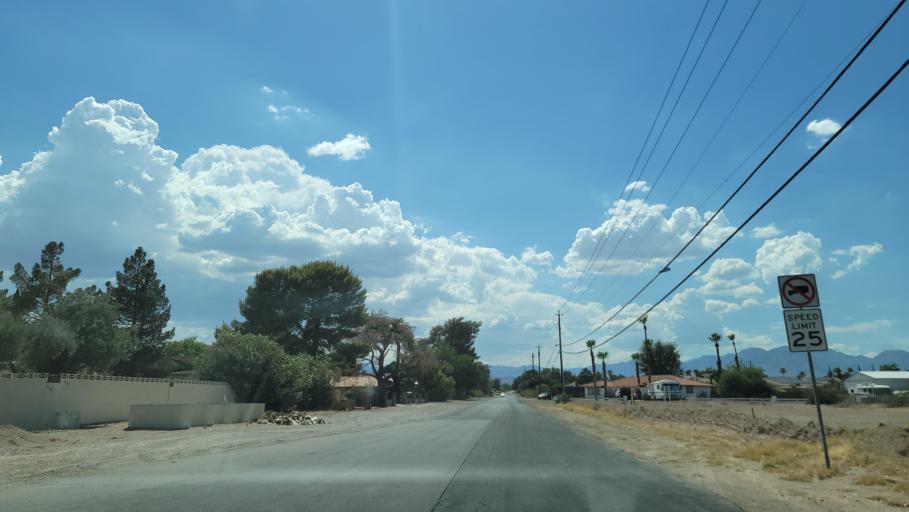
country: US
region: Nevada
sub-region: Clark County
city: Spring Valley
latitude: 36.1386
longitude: -115.2261
